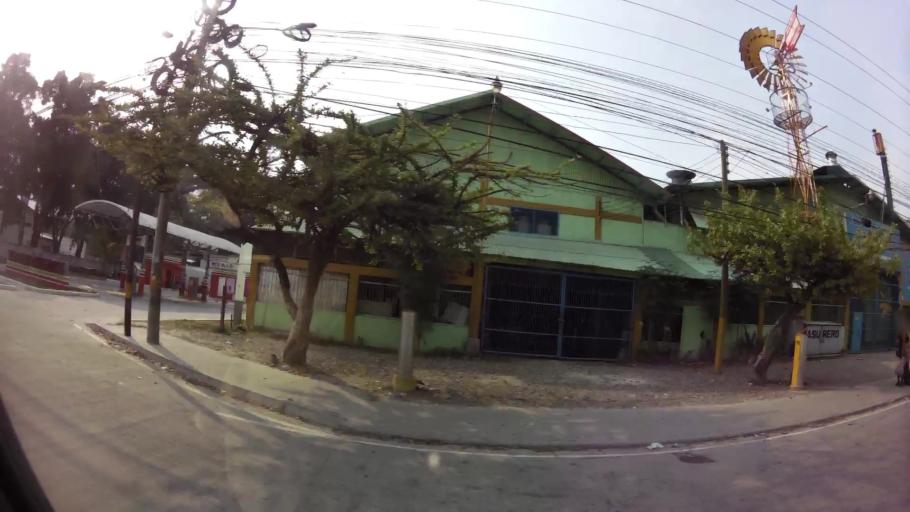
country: HN
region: Cortes
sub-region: San Pedro Sula
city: Pena Blanca
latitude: 15.5475
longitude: -88.0101
